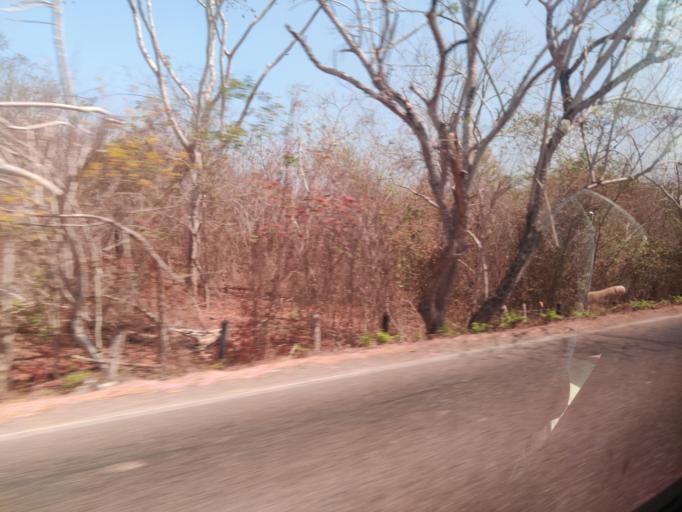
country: CO
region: Bolivar
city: Turbana
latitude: 10.2222
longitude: -75.5810
